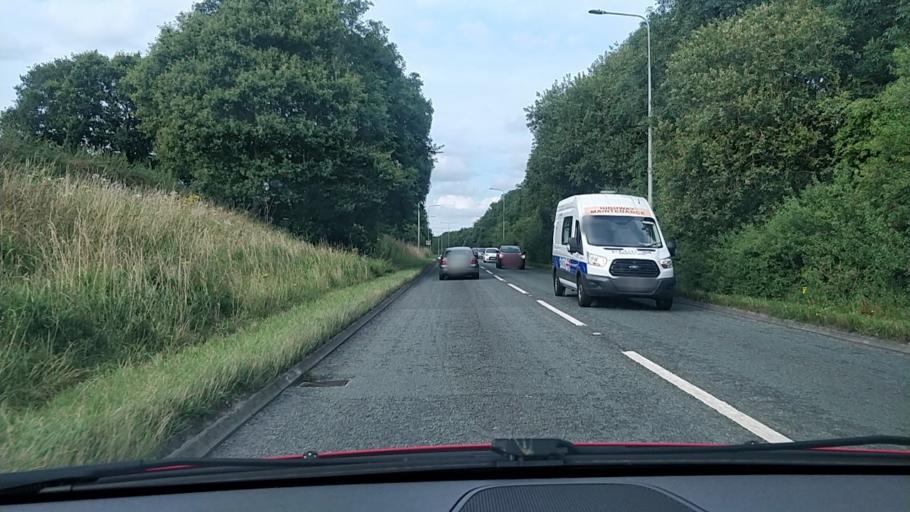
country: GB
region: Wales
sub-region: County of Flintshire
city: Penyffordd
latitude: 53.1509
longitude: -3.0475
